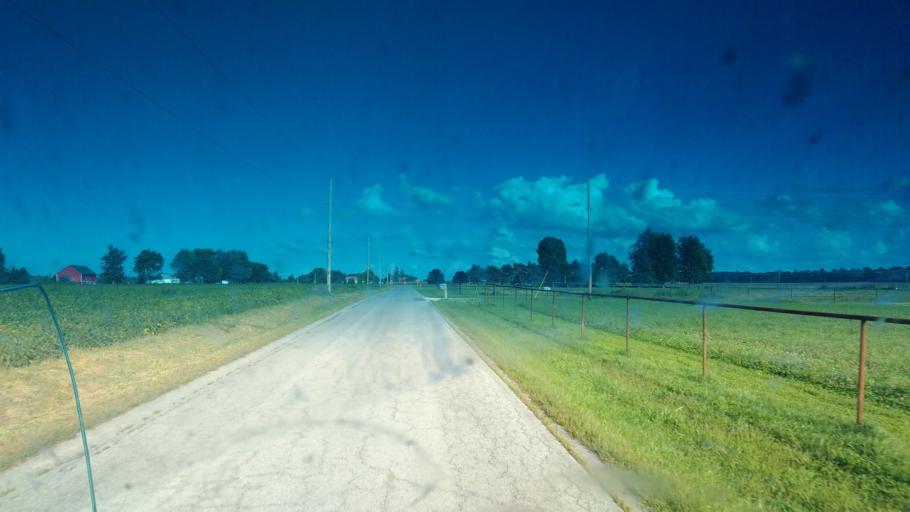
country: US
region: Ohio
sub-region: Hancock County
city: Arlington
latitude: 40.9356
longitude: -83.6554
